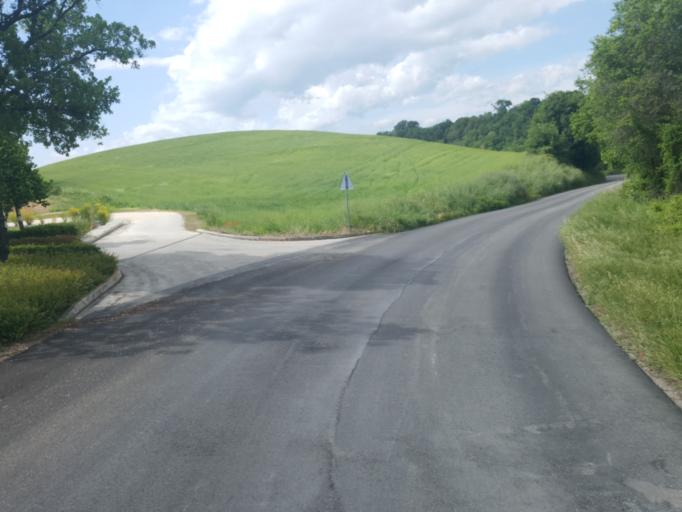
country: IT
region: The Marches
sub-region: Provincia di Macerata
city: Pollenza
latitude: 43.2501
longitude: 13.3687
